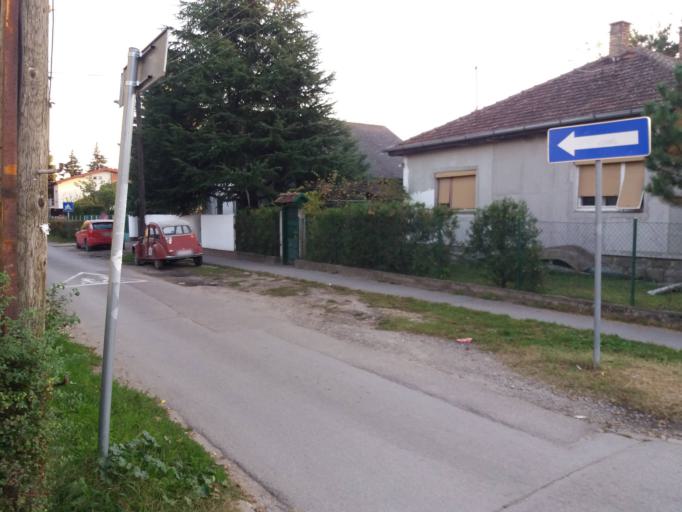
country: RS
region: Autonomna Pokrajina Vojvodina
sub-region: Severnobacki Okrug
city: Subotica
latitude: 46.1046
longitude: 19.6808
